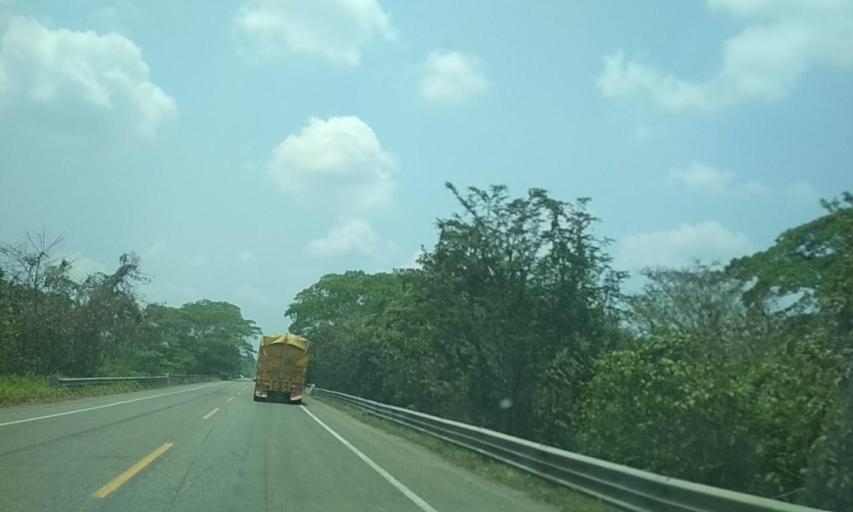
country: MX
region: Tabasco
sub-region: Huimanguillo
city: Francisco Rueda
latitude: 17.7354
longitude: -93.9743
